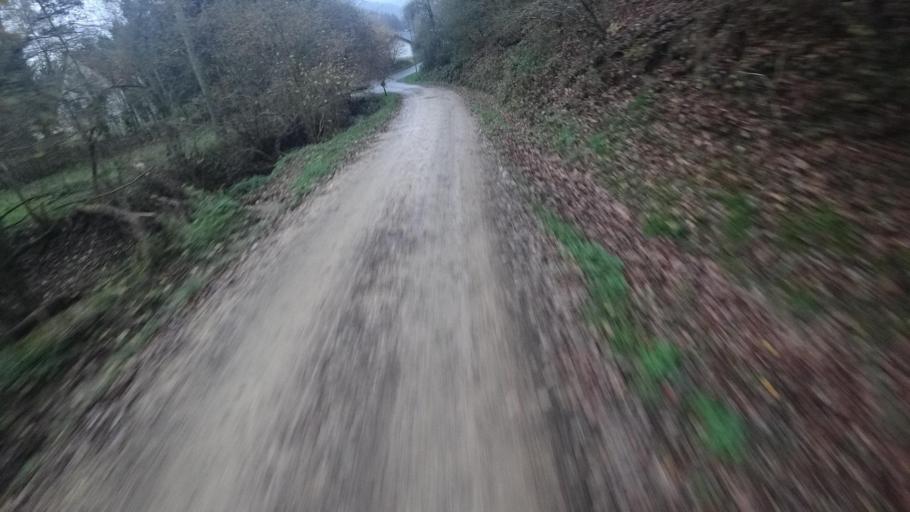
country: DE
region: Rheinland-Pfalz
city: Heckenbach
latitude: 50.4853
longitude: 7.0602
